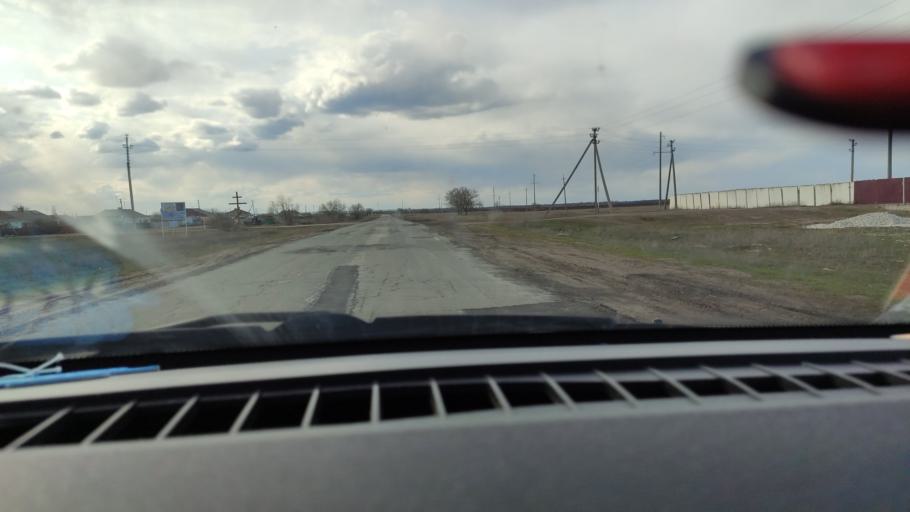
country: RU
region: Saratov
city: Rovnoye
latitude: 51.0618
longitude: 46.0203
